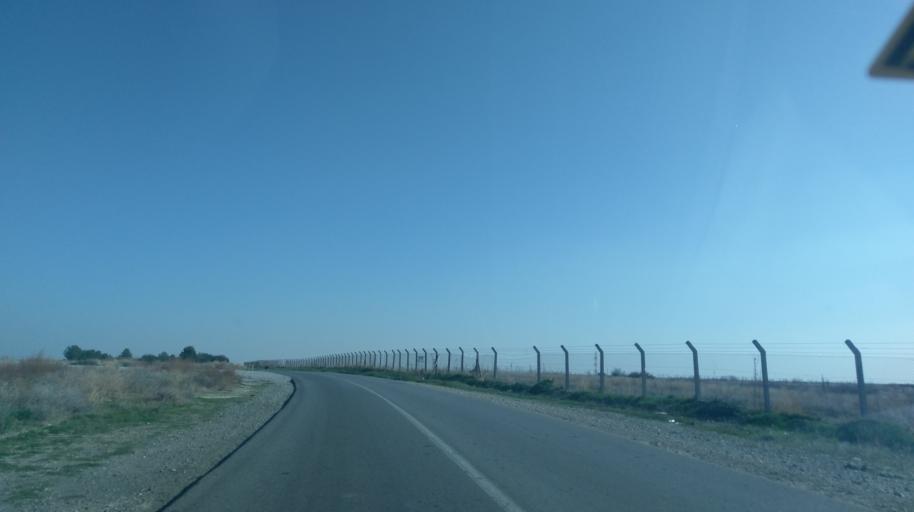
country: CY
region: Larnaka
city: Athienou
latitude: 35.1558
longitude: 33.5101
